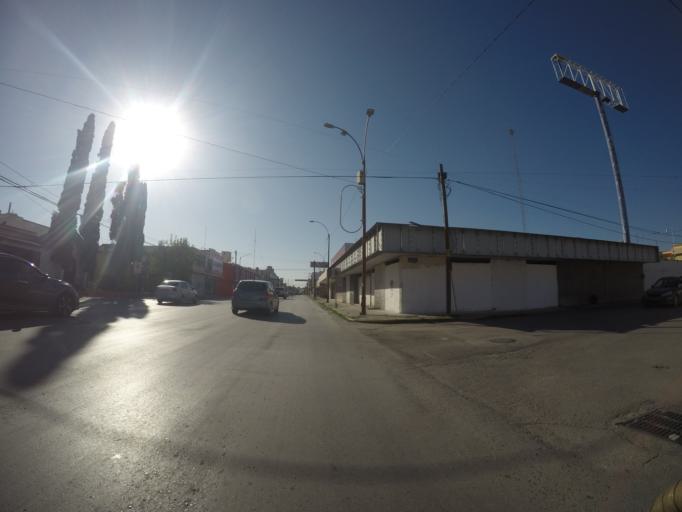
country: MX
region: Chihuahua
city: Ciudad Juarez
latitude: 31.7385
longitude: -106.4710
